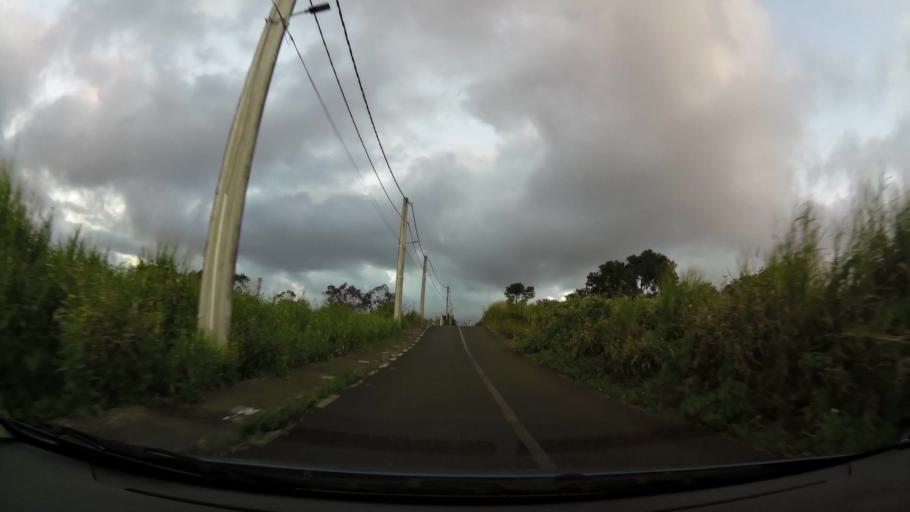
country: MU
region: Plaines Wilhems
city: Curepipe
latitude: -20.2980
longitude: 57.5319
